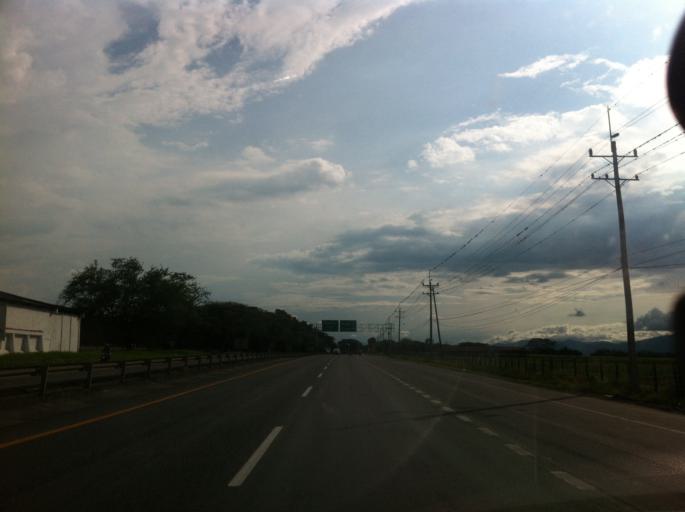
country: CO
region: Valle del Cauca
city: Buga
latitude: 3.9314
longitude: -76.2839
